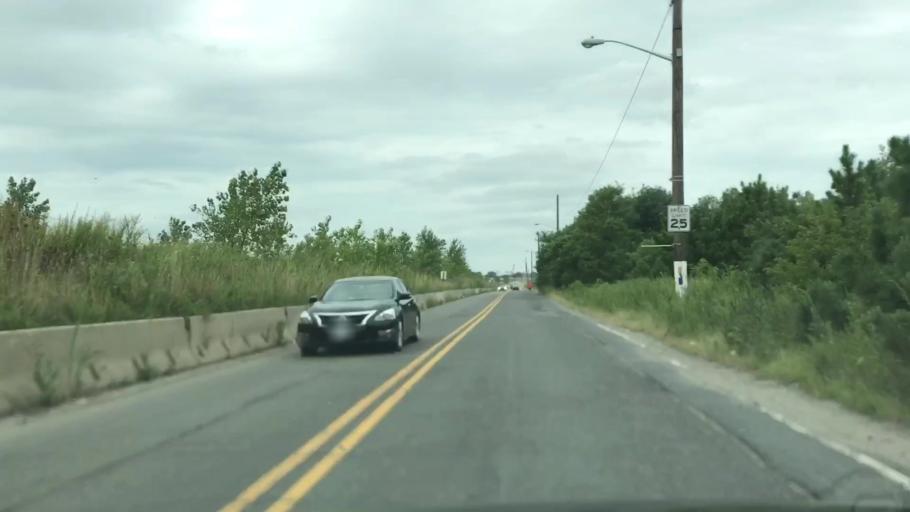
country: US
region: New Jersey
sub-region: Hudson County
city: Bayonne
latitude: 40.6682
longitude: -74.0900
